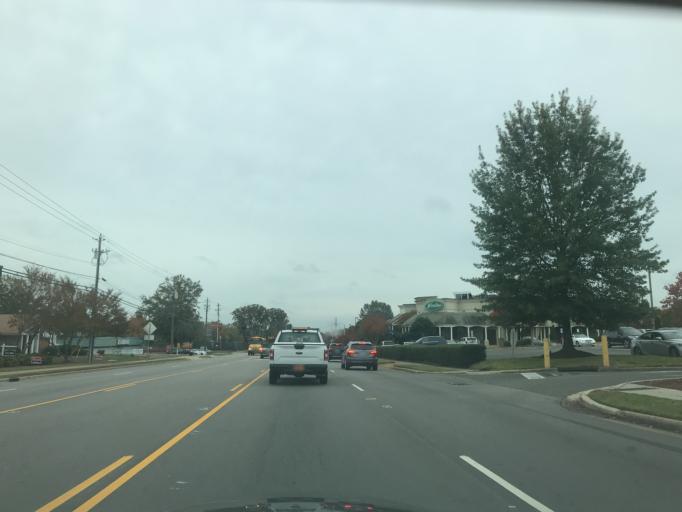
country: US
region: North Carolina
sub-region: Wake County
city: West Raleigh
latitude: 35.8705
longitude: -78.6215
